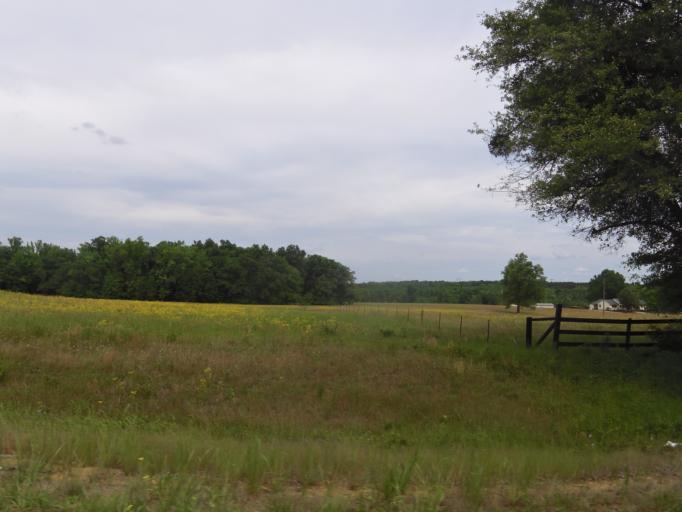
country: US
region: Georgia
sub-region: McDuffie County
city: Thomson
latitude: 33.3802
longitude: -82.4709
